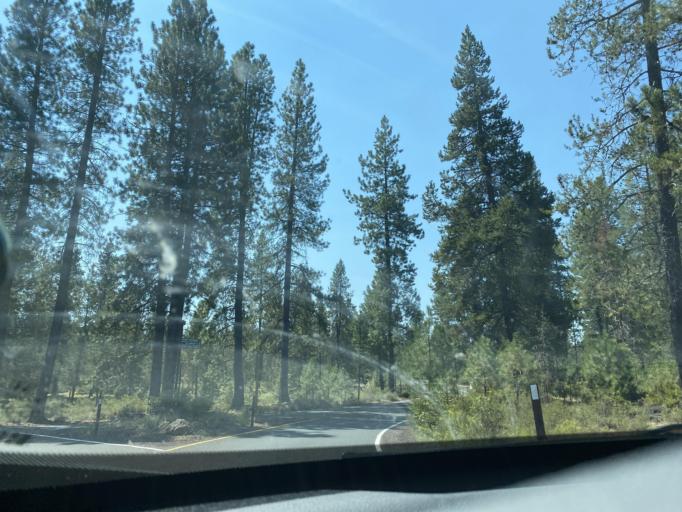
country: US
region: Oregon
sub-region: Deschutes County
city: Sunriver
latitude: 43.8921
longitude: -121.4247
